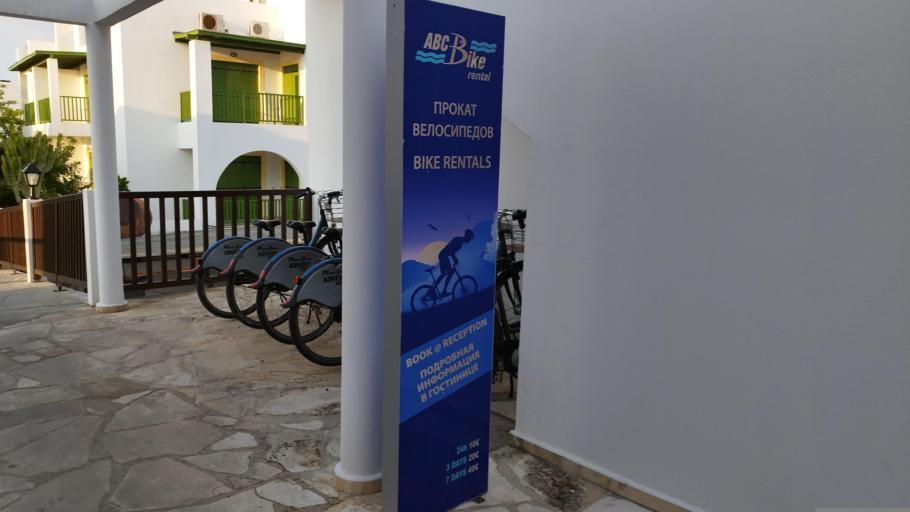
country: CY
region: Pafos
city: Paphos
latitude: 34.7698
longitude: 32.4063
